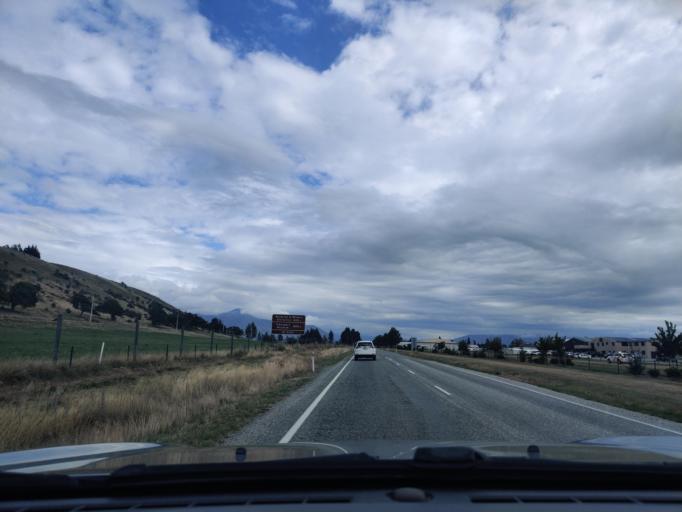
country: NZ
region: Otago
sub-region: Queenstown-Lakes District
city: Wanaka
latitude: -44.7264
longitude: 169.2481
